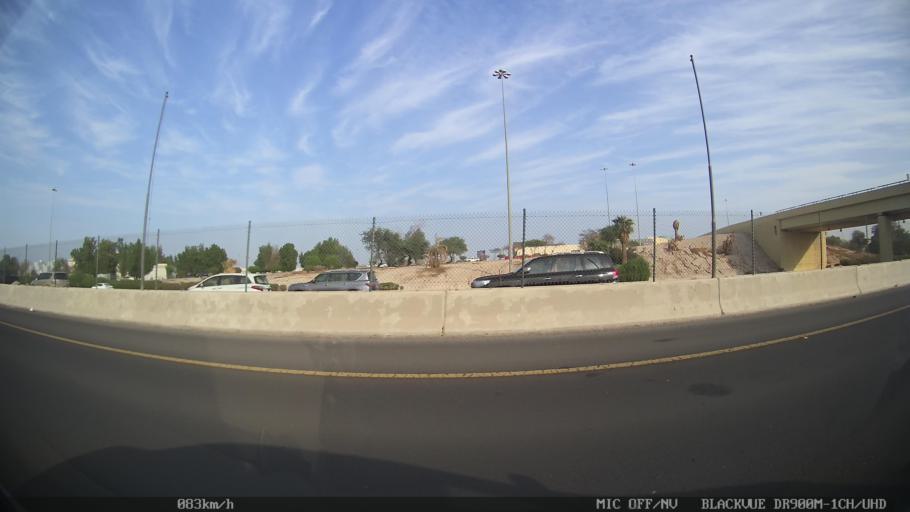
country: KW
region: Al Farwaniyah
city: Janub as Surrah
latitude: 29.2690
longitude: 47.9874
